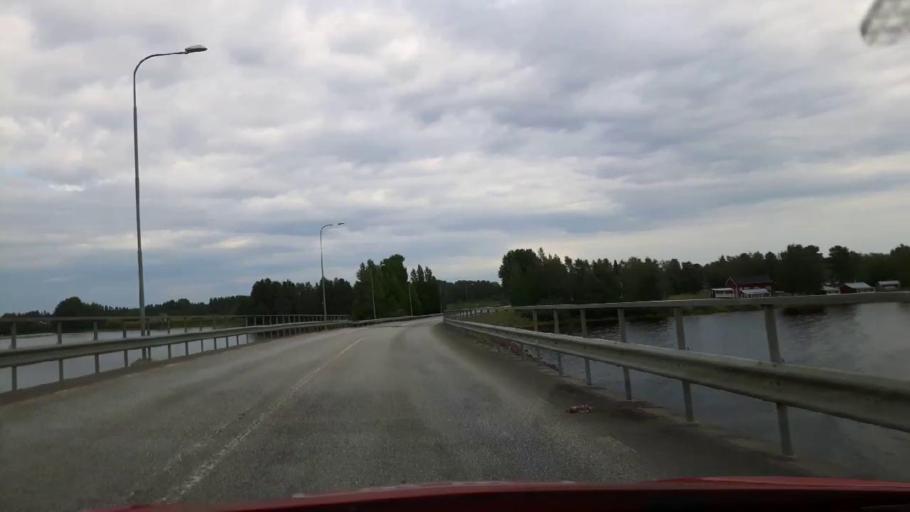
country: SE
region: Jaemtland
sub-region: Stroemsunds Kommun
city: Stroemsund
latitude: 63.6019
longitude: 15.3549
